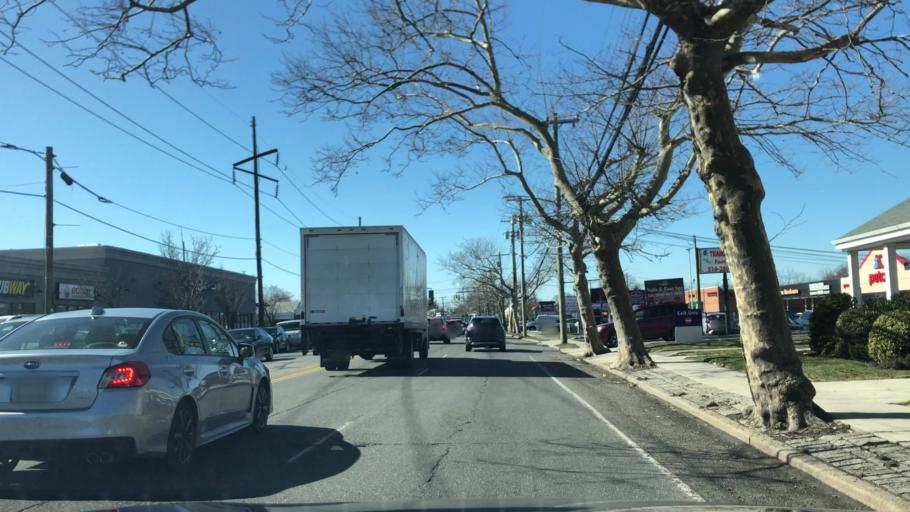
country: US
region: New York
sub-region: Nassau County
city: Malverne
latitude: 40.6902
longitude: -73.6853
